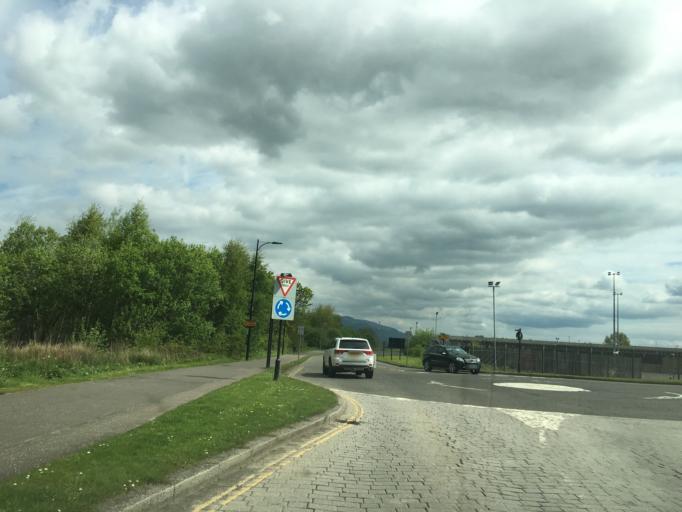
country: GB
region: Scotland
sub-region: Stirling
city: Stirling
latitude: 56.1185
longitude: -3.9277
